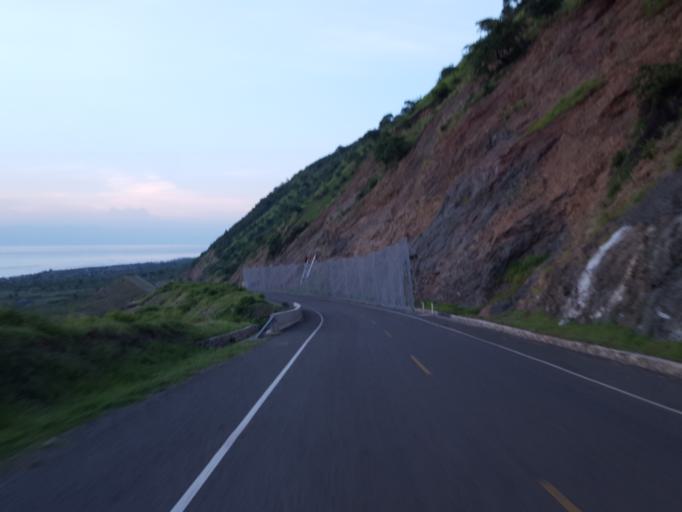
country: UG
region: Western Region
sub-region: Kibale District
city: Kagadi
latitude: 1.2435
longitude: 30.7584
